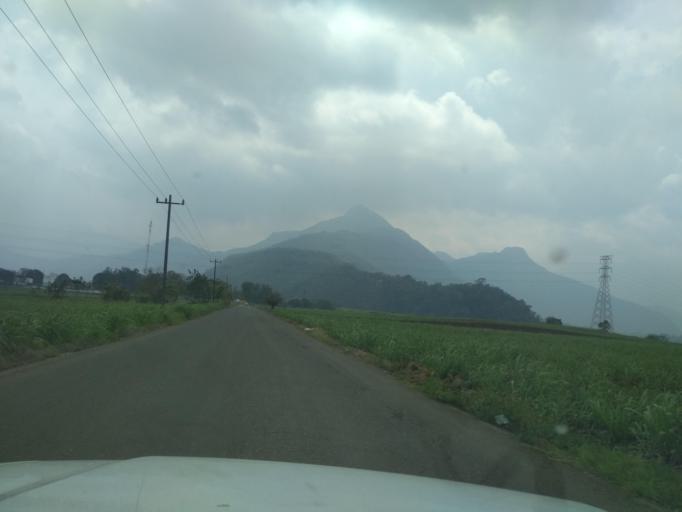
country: MX
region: Veracruz
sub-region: Cordoba
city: San Jose de Tapia
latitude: 18.8396
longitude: -96.9783
